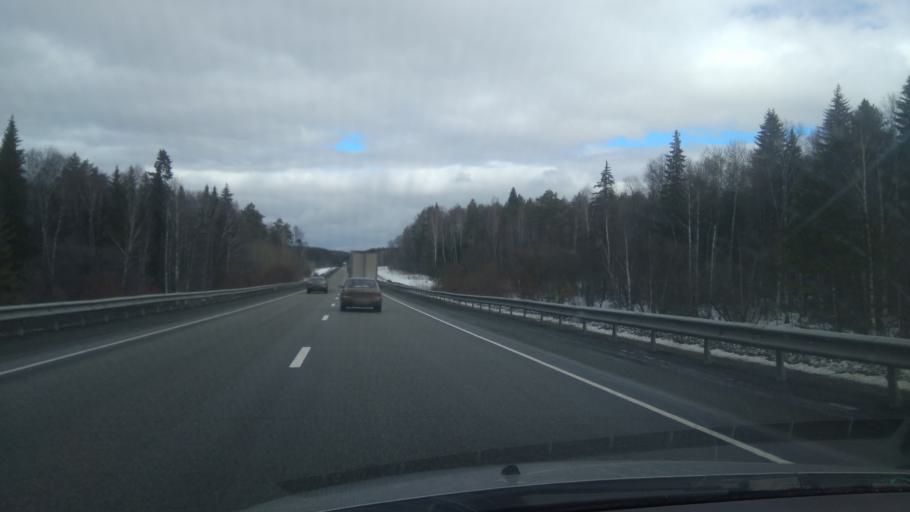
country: RU
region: Sverdlovsk
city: Bisert'
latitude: 56.8207
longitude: 58.7582
